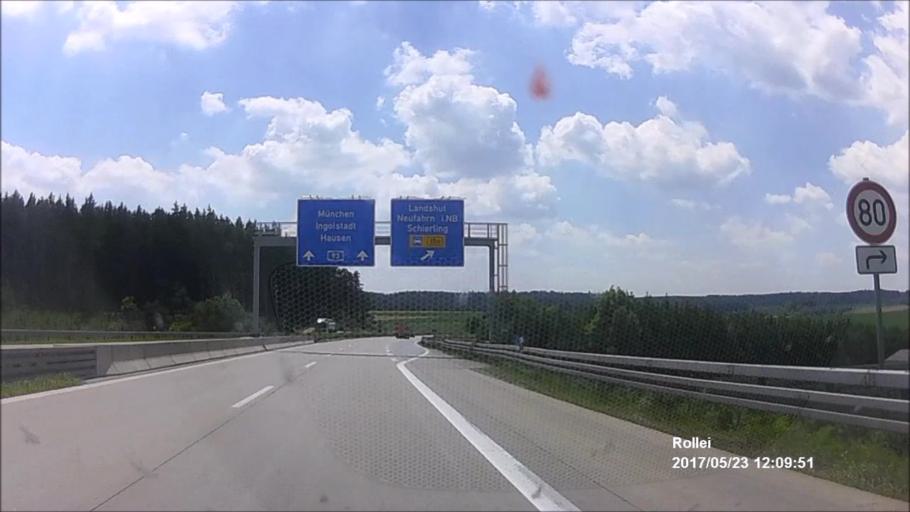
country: DE
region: Bavaria
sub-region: Lower Bavaria
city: Bad Abbach
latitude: 48.8958
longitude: 12.0783
